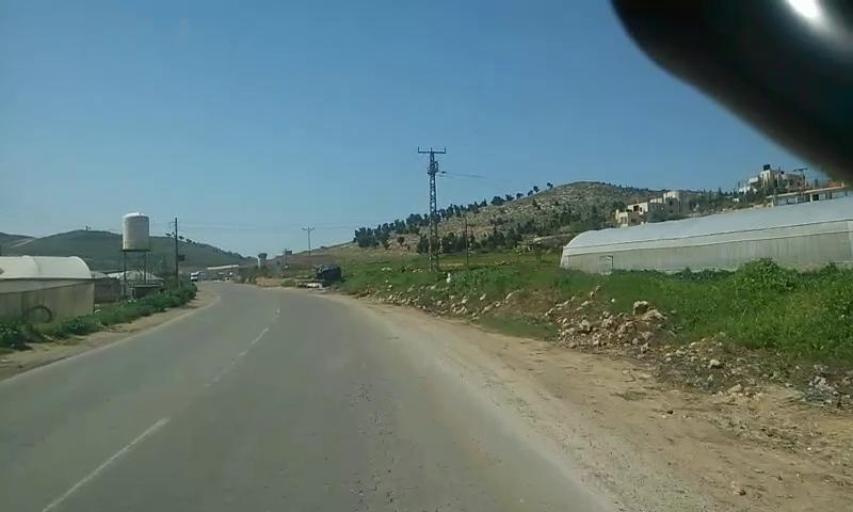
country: PS
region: West Bank
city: Ar Rihiyah
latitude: 31.4862
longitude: 35.0568
